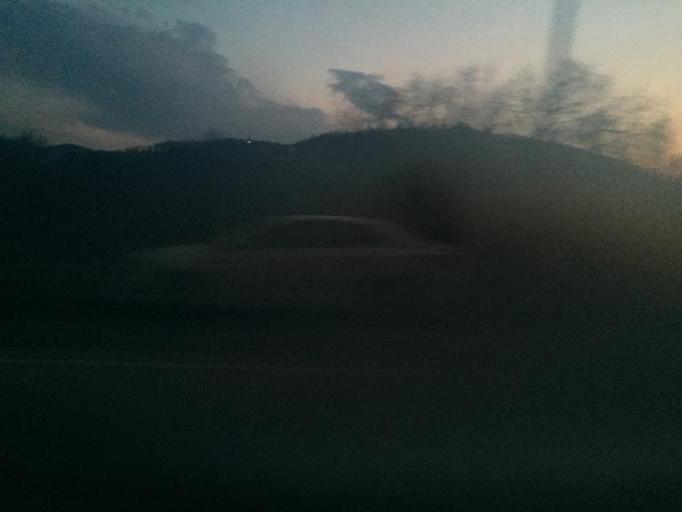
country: TR
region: Samsun
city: Kavak
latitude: 41.1374
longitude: 36.1247
